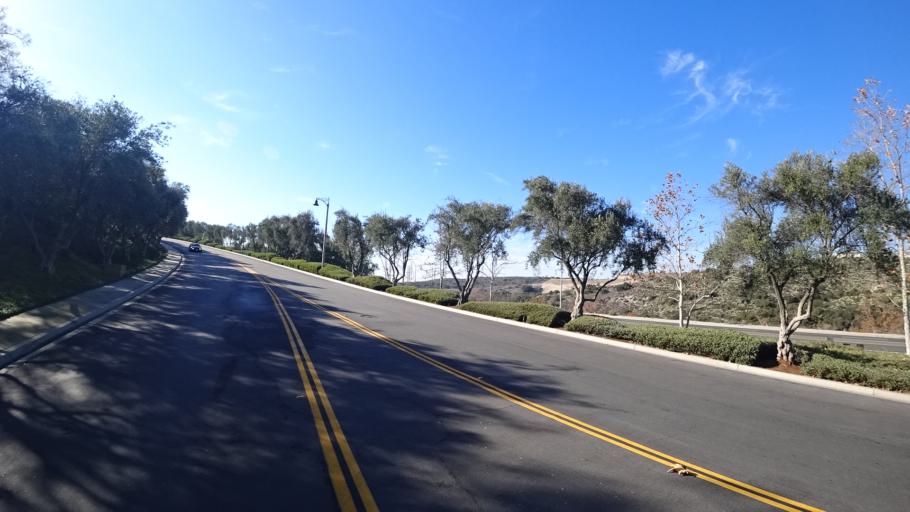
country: US
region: California
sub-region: Orange County
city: Portola Hills
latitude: 33.6644
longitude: -117.6311
